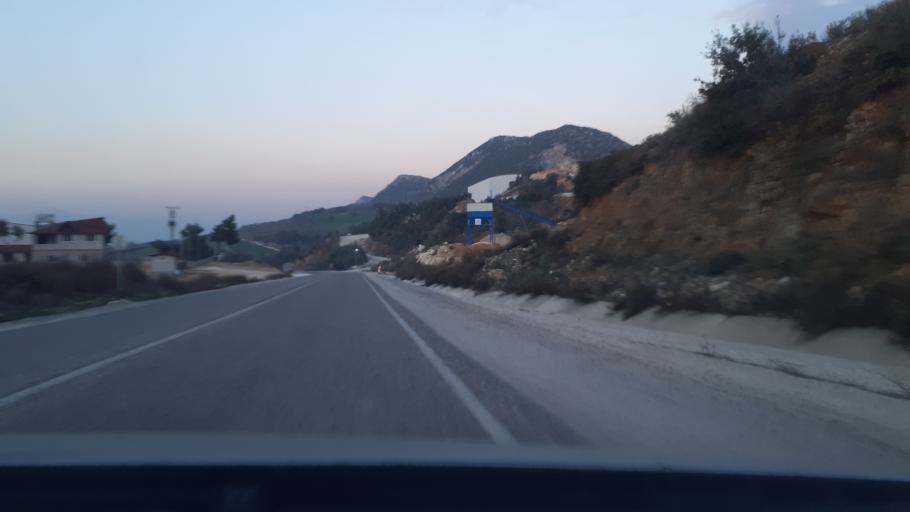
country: TR
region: Hatay
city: Dursunlu
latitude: 36.1738
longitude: 36.1867
